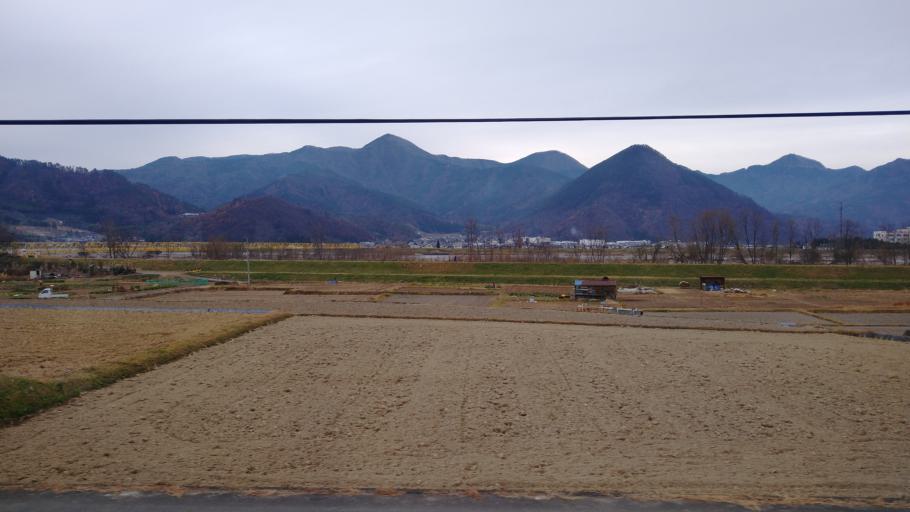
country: JP
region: Nagano
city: Ueda
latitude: 36.4506
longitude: 138.1861
